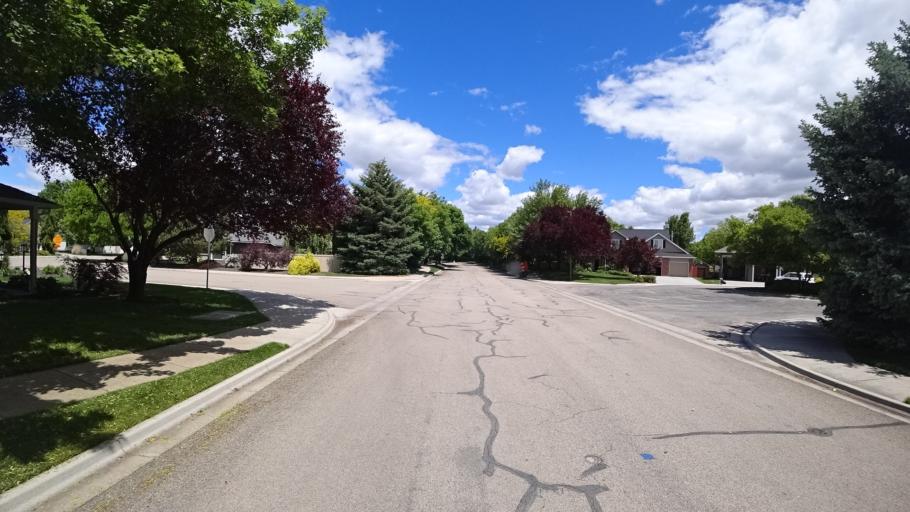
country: US
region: Idaho
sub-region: Ada County
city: Eagle
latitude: 43.6601
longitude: -116.3605
